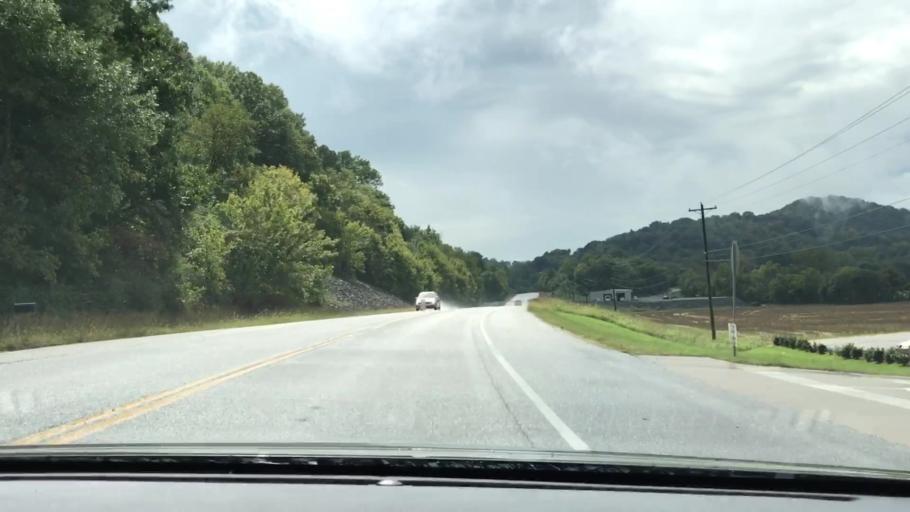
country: US
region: Tennessee
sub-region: Smith County
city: Carthage
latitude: 36.3136
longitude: -85.9709
